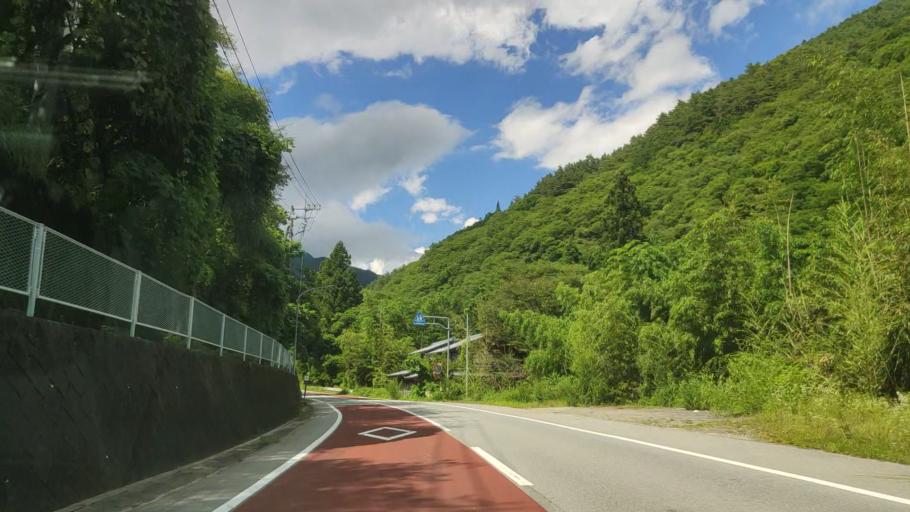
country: JP
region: Yamanashi
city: Enzan
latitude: 35.7816
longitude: 138.7393
